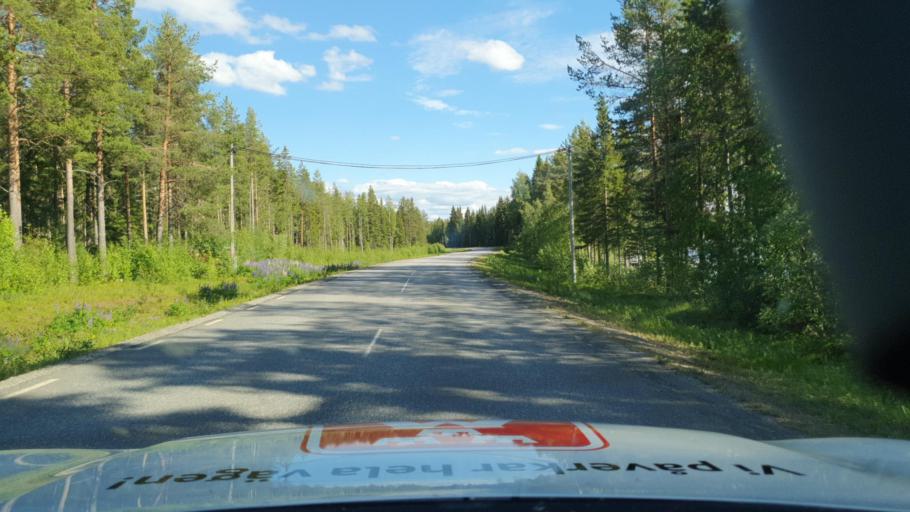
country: SE
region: Vaesterbotten
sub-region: Norsjo Kommun
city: Norsjoe
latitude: 64.8392
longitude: 19.7638
